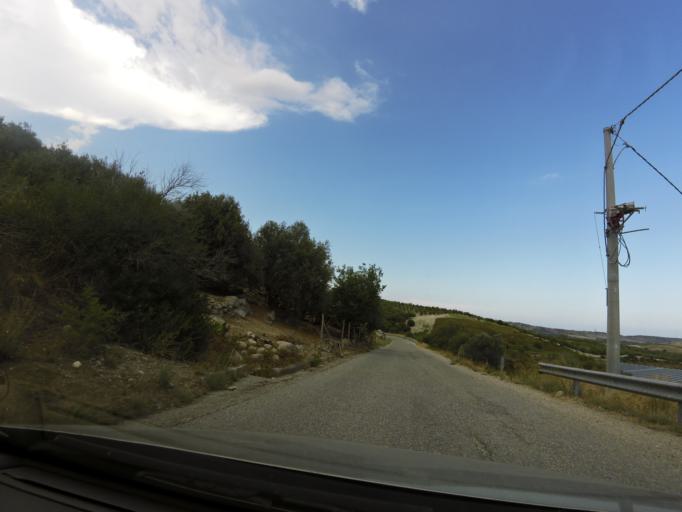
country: IT
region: Calabria
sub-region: Provincia di Reggio Calabria
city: Camini
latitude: 38.4277
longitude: 16.5164
